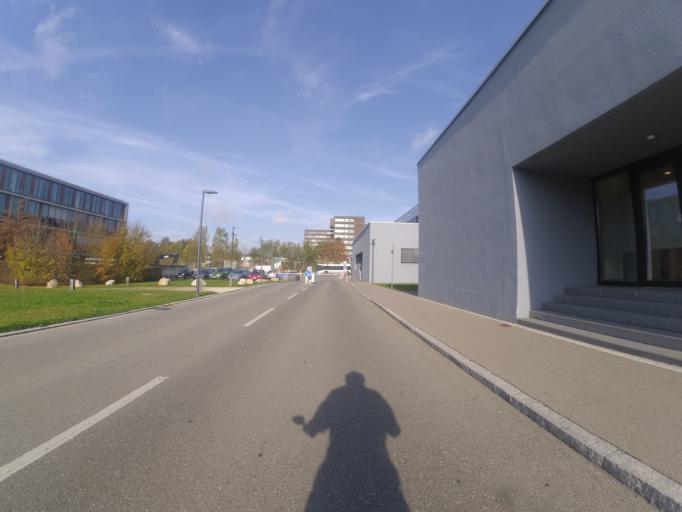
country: DE
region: Baden-Wuerttemberg
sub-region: Tuebingen Region
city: Dornstadt
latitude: 48.4227
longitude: 9.9499
